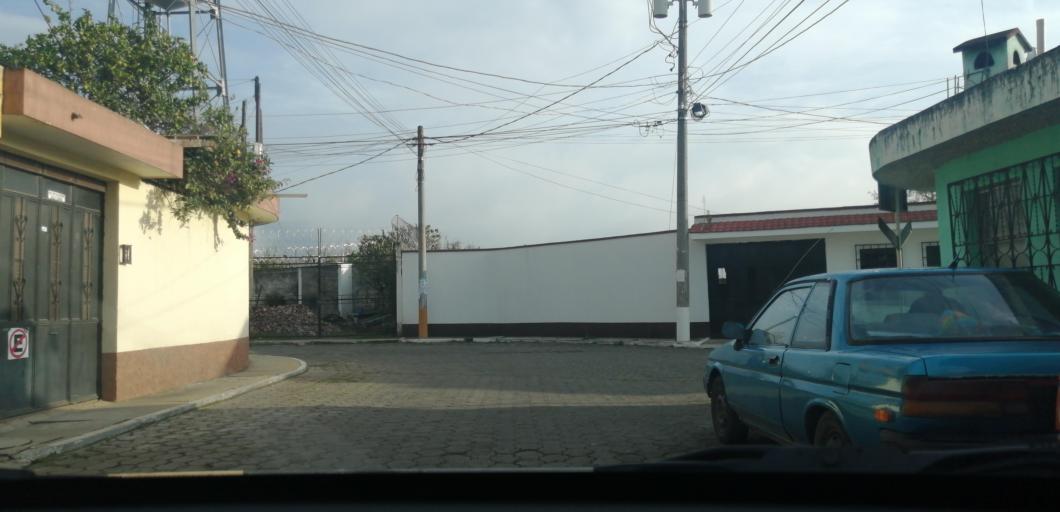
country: GT
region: Quetzaltenango
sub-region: Municipio de La Esperanza
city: La Esperanza
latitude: 14.8663
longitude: -91.5436
